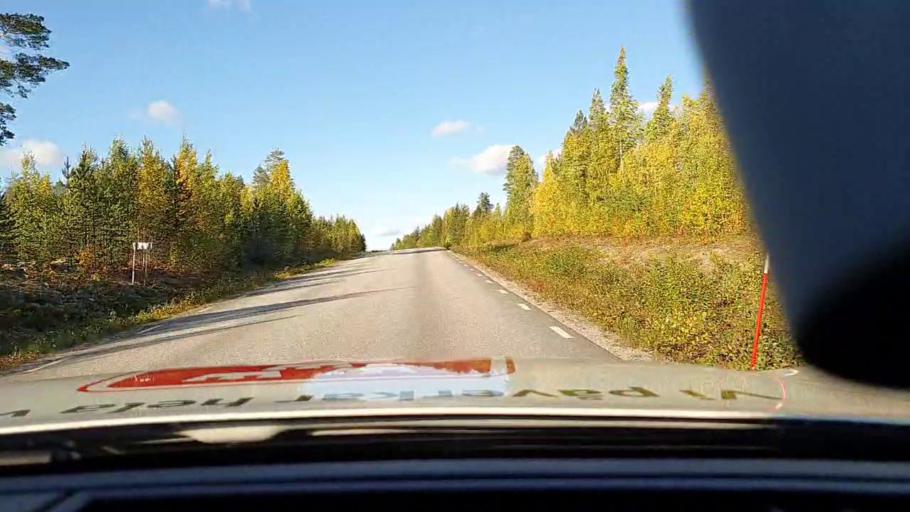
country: SE
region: Norrbotten
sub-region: Pitea Kommun
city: Norrfjarden
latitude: 65.4945
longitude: 21.4743
